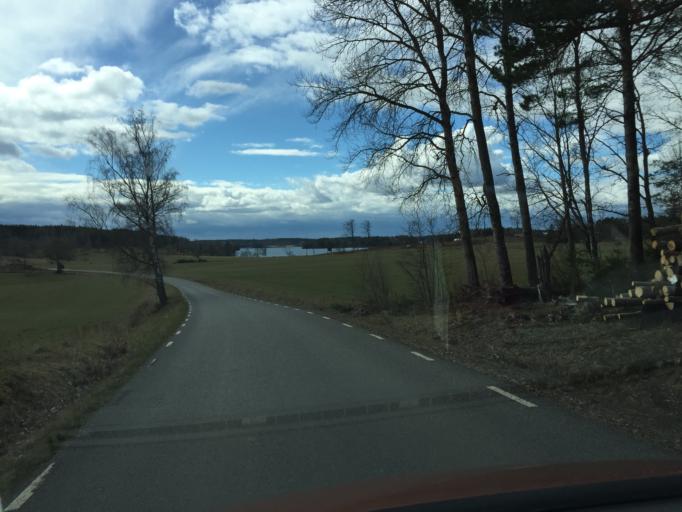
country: SE
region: Soedermanland
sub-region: Nykopings Kommun
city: Stigtomta
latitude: 58.9765
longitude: 16.9009
